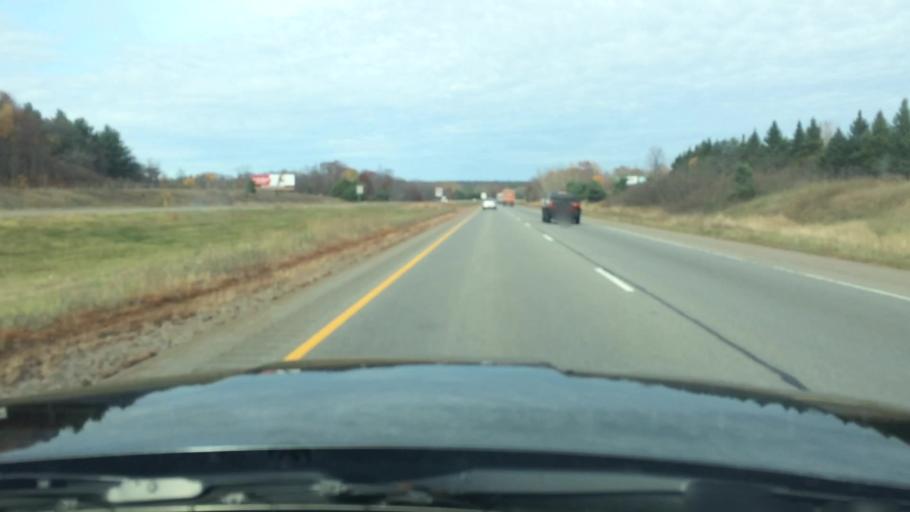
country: US
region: Wisconsin
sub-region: Marathon County
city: Mosinee
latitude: 44.7973
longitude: -89.6790
